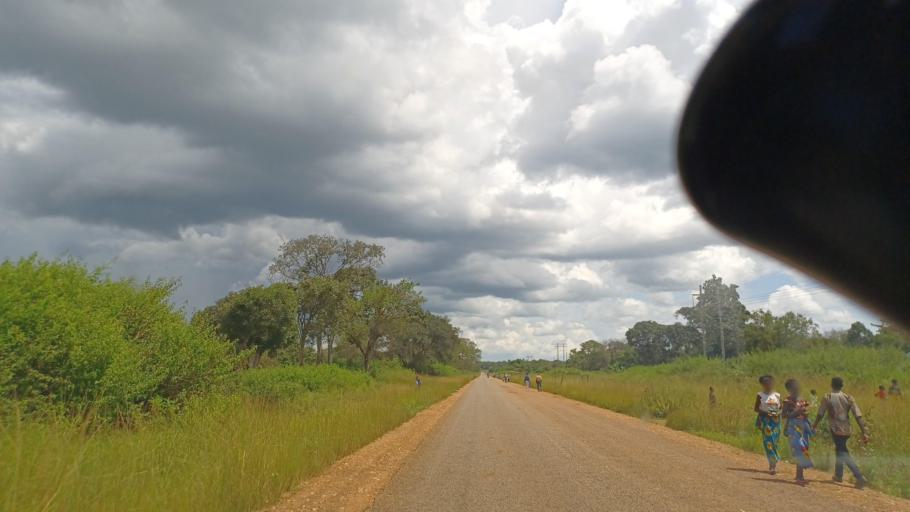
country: ZM
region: North-Western
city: Solwezi
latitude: -12.7702
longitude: 26.0152
